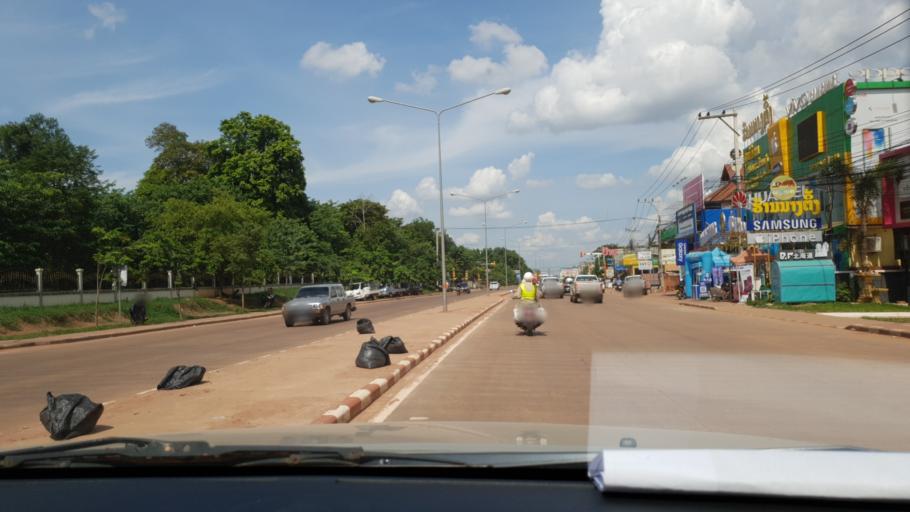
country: LA
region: Vientiane
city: Vientiane
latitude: 18.0341
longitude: 102.6332
